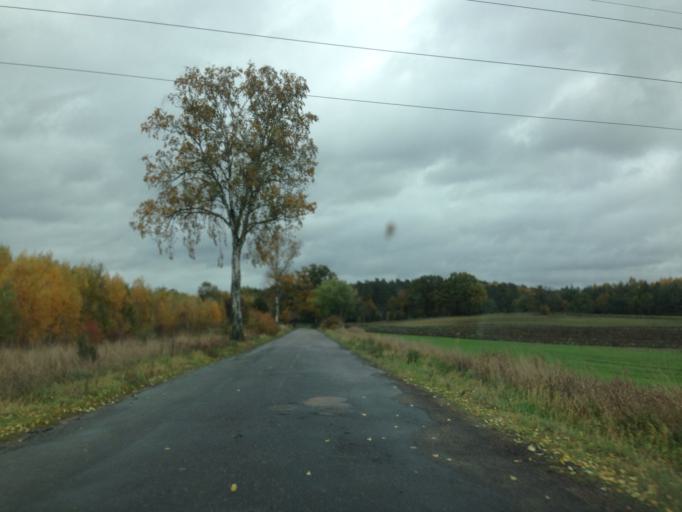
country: PL
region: Pomeranian Voivodeship
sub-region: Powiat kwidzynski
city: Ryjewo
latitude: 53.8363
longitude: 19.0113
